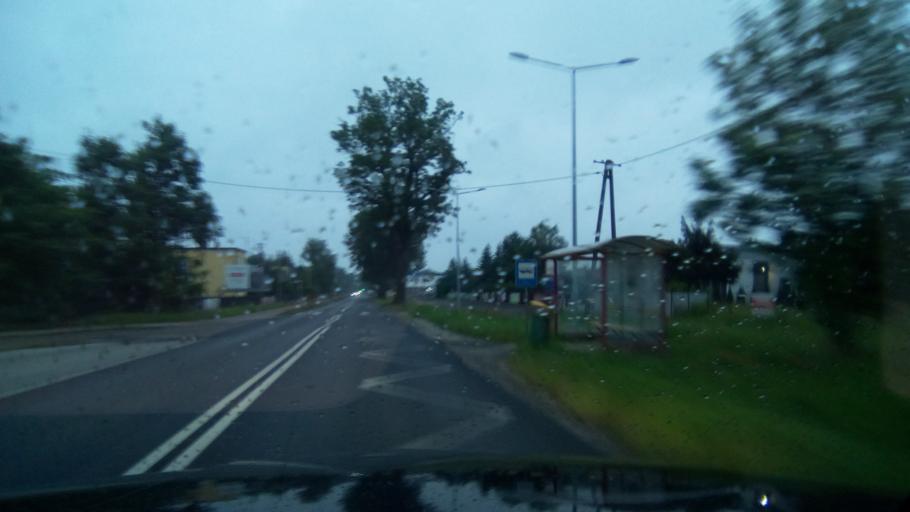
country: PL
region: Greater Poland Voivodeship
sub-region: Powiat poznanski
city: Kobylnica
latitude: 52.4396
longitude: 17.0748
